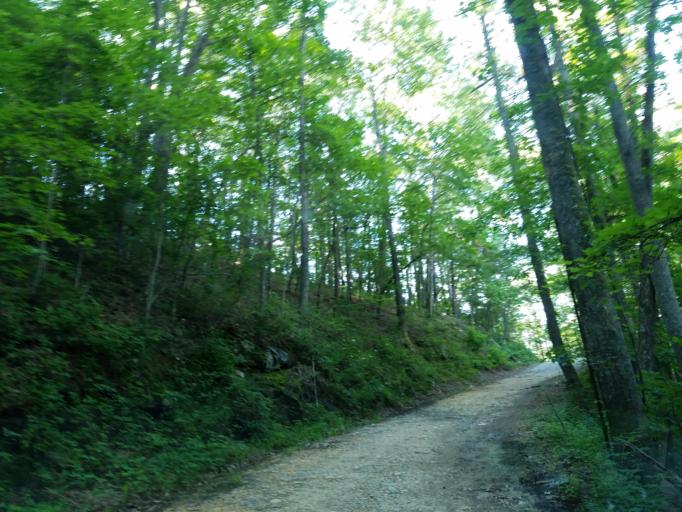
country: US
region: Georgia
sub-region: Dawson County
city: Dawsonville
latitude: 34.5913
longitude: -84.2049
